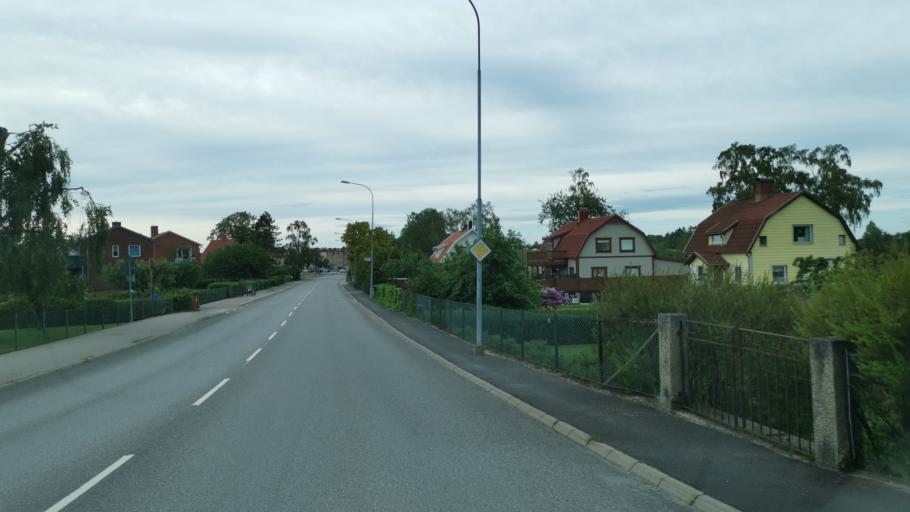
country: SE
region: Vaestra Goetaland
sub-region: Vanersborgs Kommun
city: Vargon
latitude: 58.3615
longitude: 12.3571
